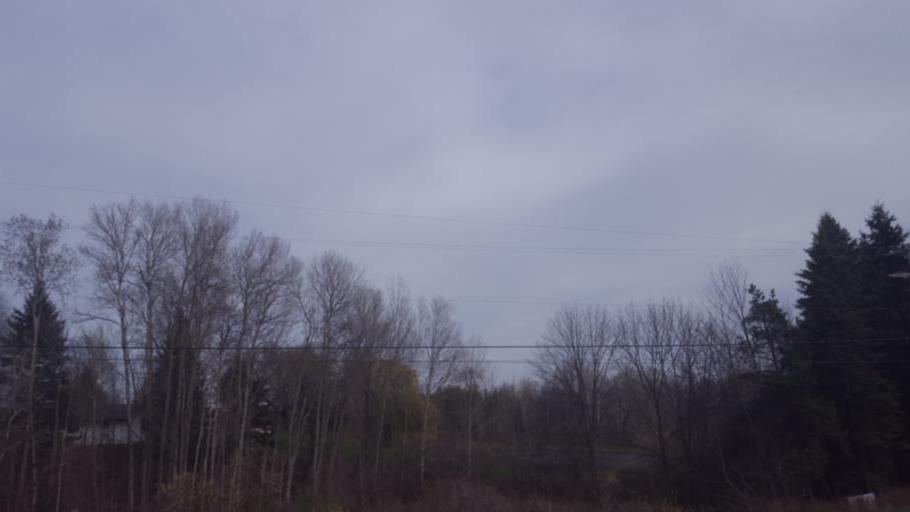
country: US
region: Michigan
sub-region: Clare County
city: Clare
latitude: 43.8577
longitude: -84.7681
